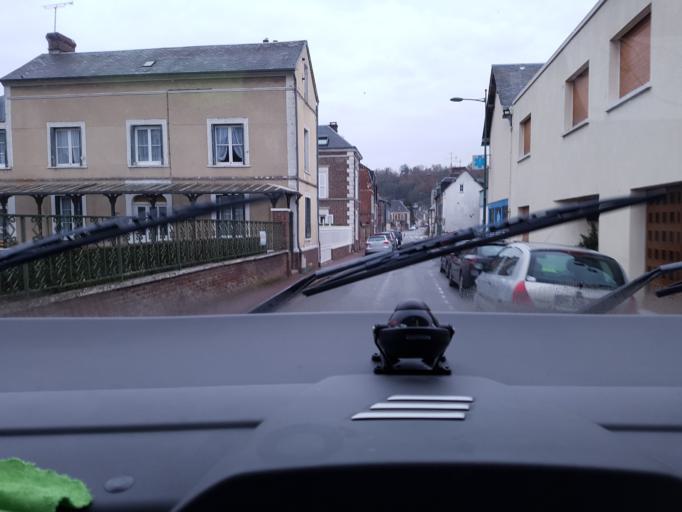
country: FR
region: Haute-Normandie
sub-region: Departement de l'Eure
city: Beaumont-le-Roger
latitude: 49.0773
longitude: 0.7753
